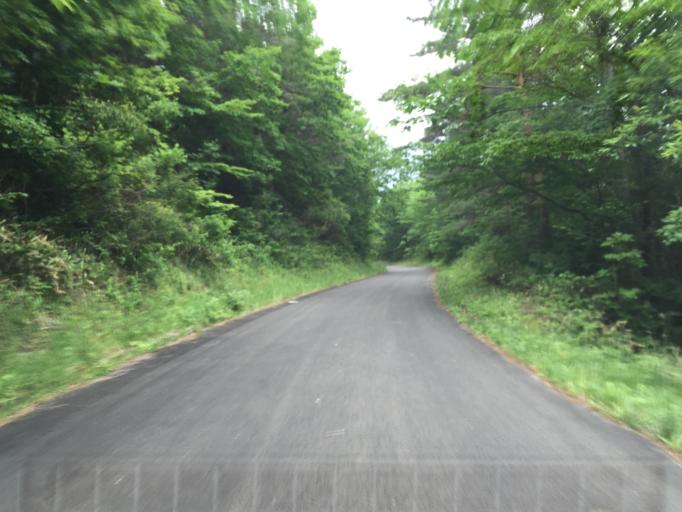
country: JP
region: Fukushima
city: Yanagawamachi-saiwaicho
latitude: 37.7906
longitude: 140.6880
